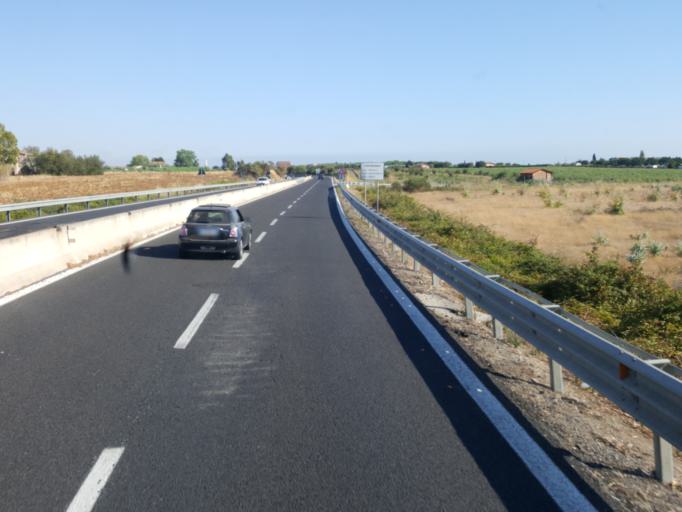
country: IT
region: Latium
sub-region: Provincia di Viterbo
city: Pescia Romana
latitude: 42.4122
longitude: 11.4760
